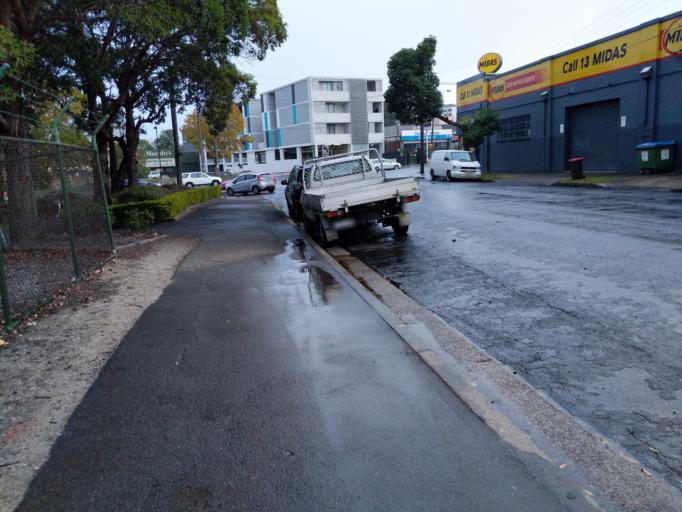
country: AU
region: New South Wales
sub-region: Ashfield
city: Croydon
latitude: -33.8688
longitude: 151.1080
